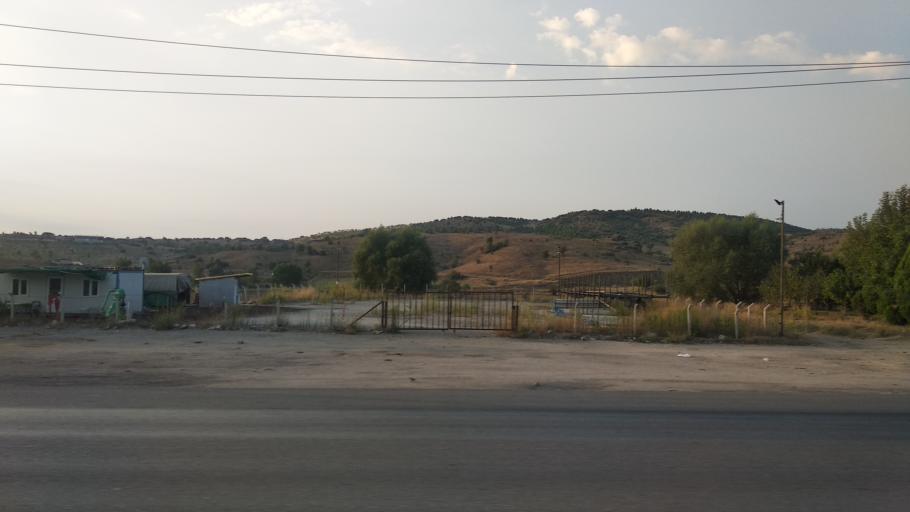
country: TR
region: Manisa
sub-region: Kula
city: Kula
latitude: 38.5450
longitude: 28.6636
